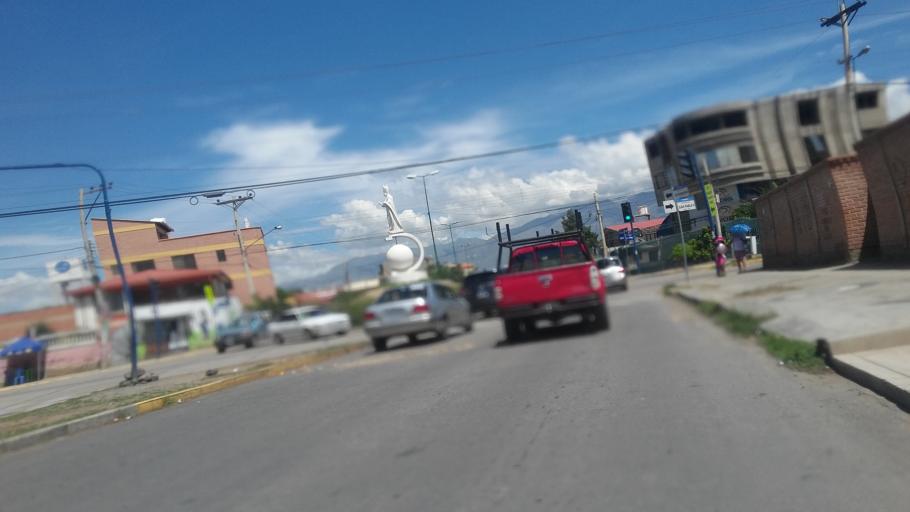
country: BO
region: Cochabamba
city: Cochabamba
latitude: -17.3860
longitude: -66.1988
